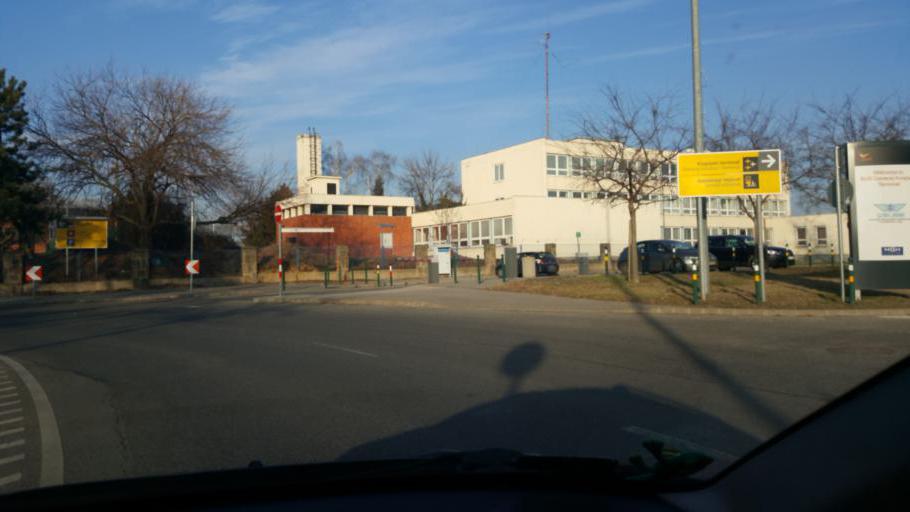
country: HU
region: Budapest
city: Budapest XVIII. keruelet
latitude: 47.4404
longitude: 19.2228
